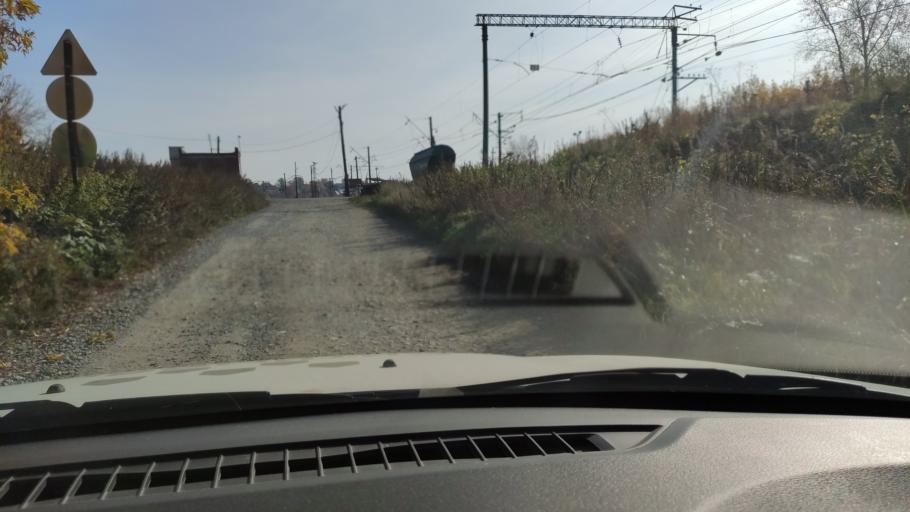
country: RU
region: Perm
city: Sylva
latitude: 58.0430
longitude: 56.7476
